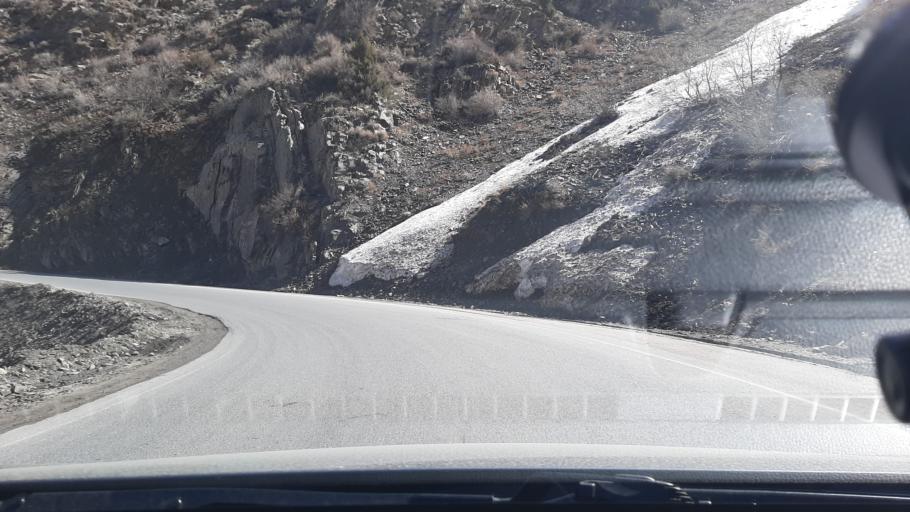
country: TJ
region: Viloyati Sughd
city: Ayni
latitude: 39.4911
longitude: 68.5536
